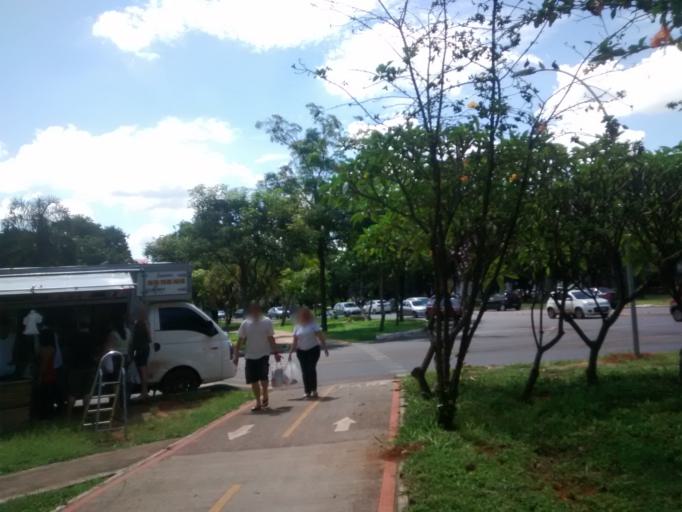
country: BR
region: Federal District
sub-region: Brasilia
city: Brasilia
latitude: -15.7725
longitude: -47.8854
